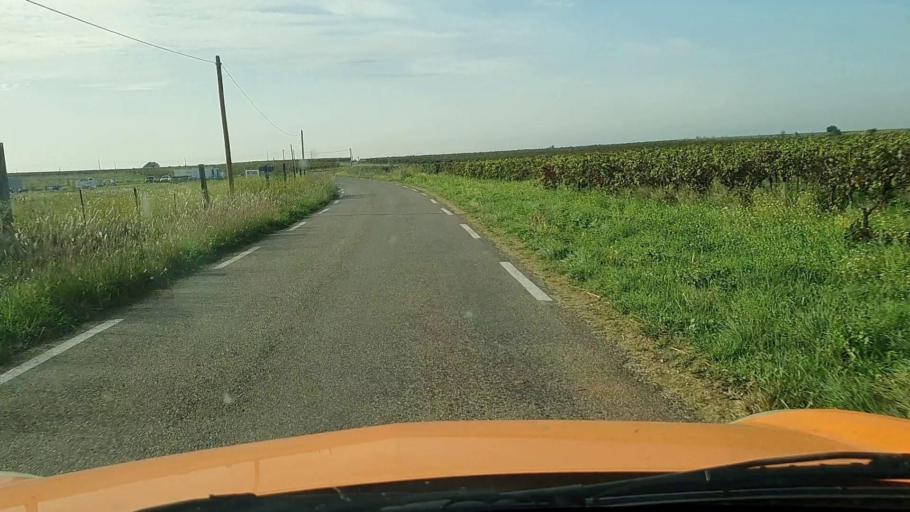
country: FR
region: Languedoc-Roussillon
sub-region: Departement du Gard
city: Beauvoisin
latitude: 43.7107
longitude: 4.3395
